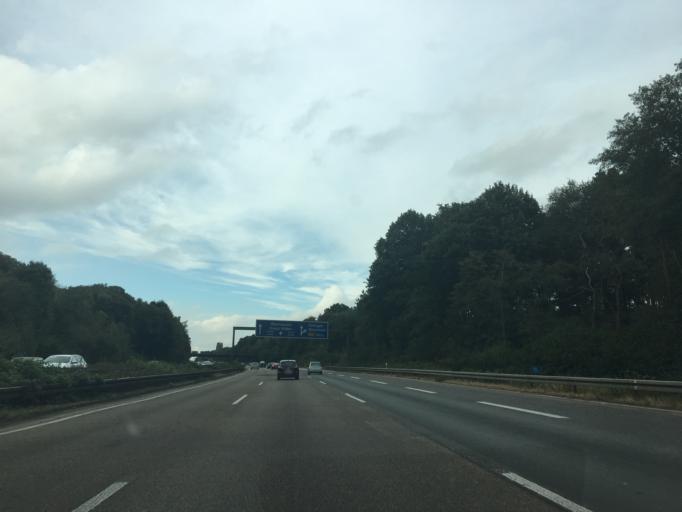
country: DE
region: North Rhine-Westphalia
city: Leichlingen
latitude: 51.1149
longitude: 6.9863
